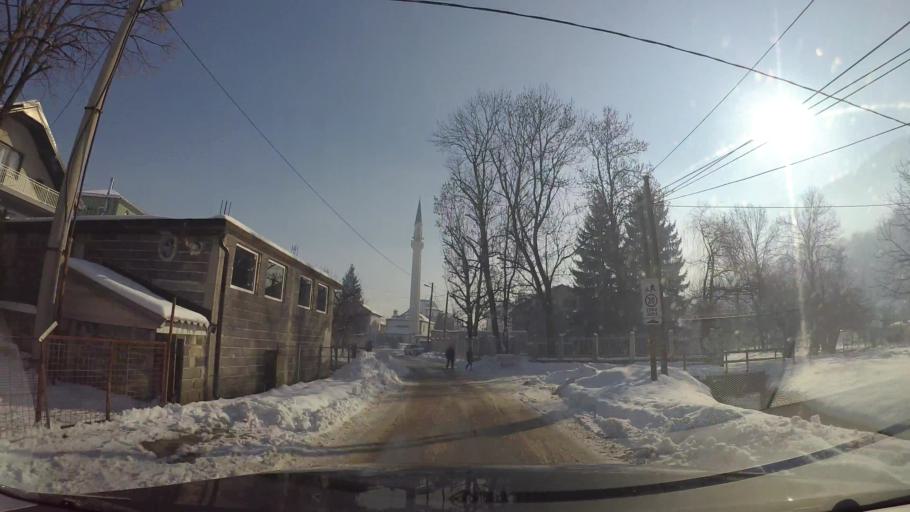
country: BA
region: Federation of Bosnia and Herzegovina
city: Gracanica
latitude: 43.8028
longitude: 18.3008
